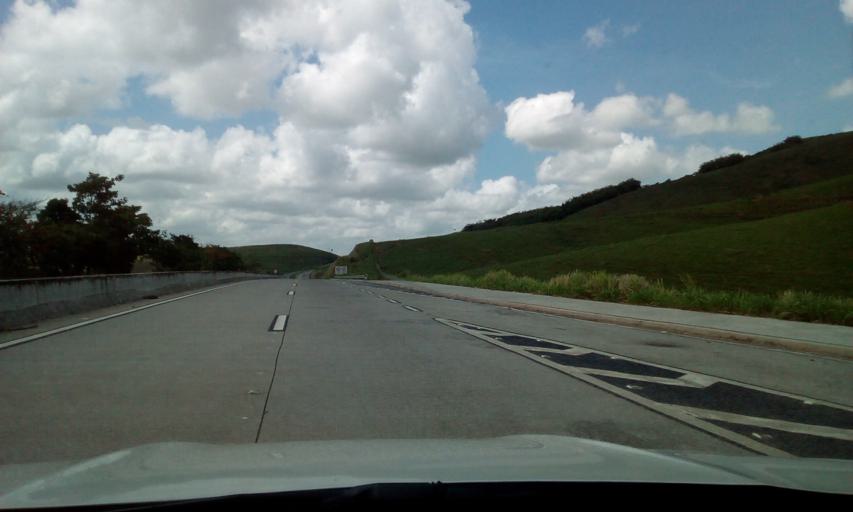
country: BR
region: Alagoas
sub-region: Flexeiras
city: Flexeiras
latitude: -9.2602
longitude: -35.7773
